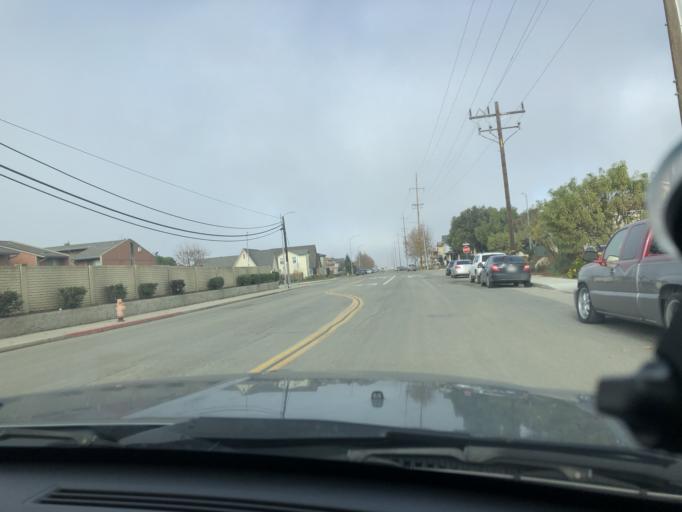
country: US
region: California
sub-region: Monterey County
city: King City
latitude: 36.2190
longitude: -121.1312
